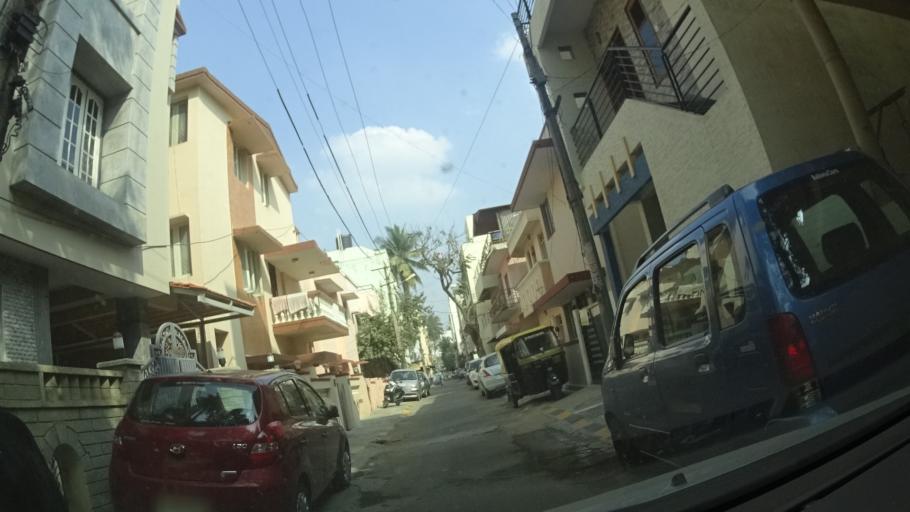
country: IN
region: Karnataka
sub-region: Bangalore Urban
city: Bangalore
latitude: 12.9429
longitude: 77.5638
